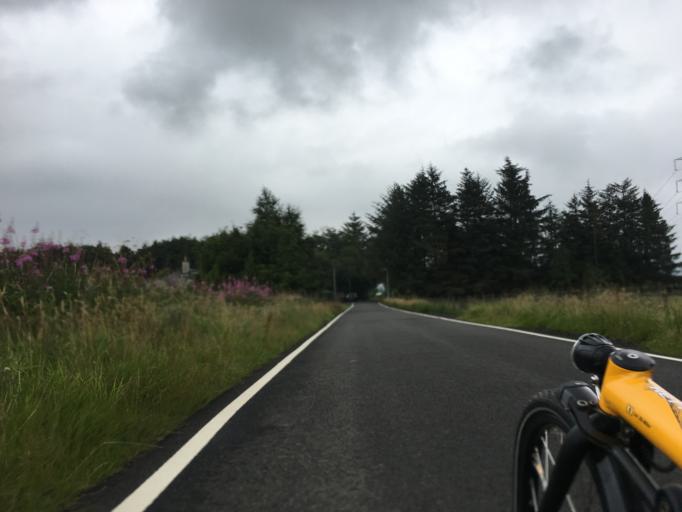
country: GB
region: Scotland
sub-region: West Lothian
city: West Calder
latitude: 55.8417
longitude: -3.5247
